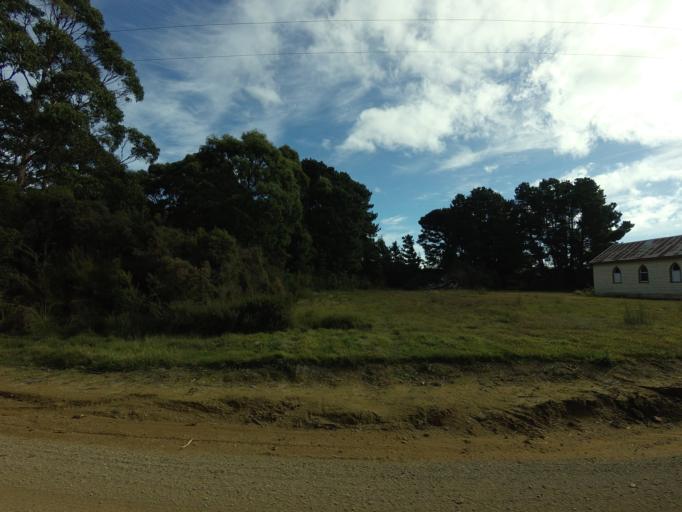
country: AU
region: Tasmania
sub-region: Clarence
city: Sandford
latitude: -43.1621
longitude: 147.7684
